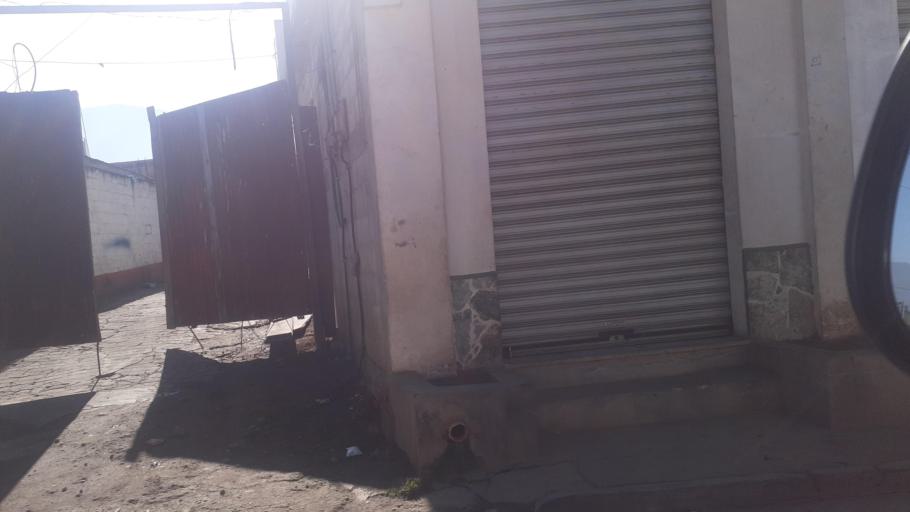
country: GT
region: Quetzaltenango
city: Cantel
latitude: 14.8188
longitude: -91.4484
